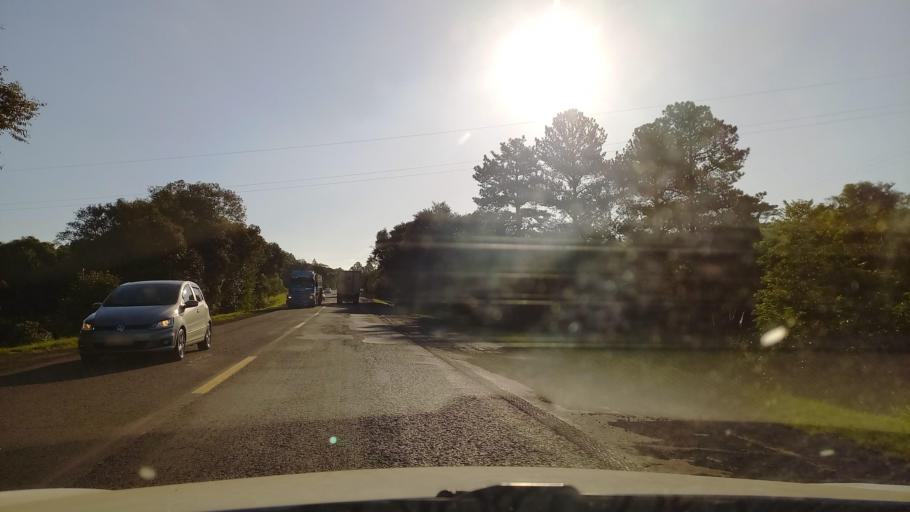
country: BR
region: Rio Grande do Sul
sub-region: Taquari
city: Taquari
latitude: -29.6982
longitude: -51.9401
